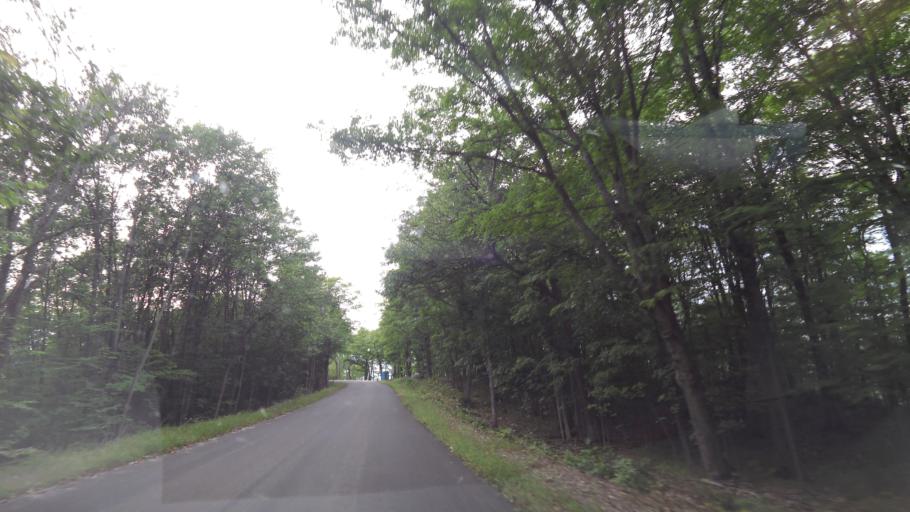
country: CA
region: Ontario
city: Bancroft
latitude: 45.0429
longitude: -78.5005
